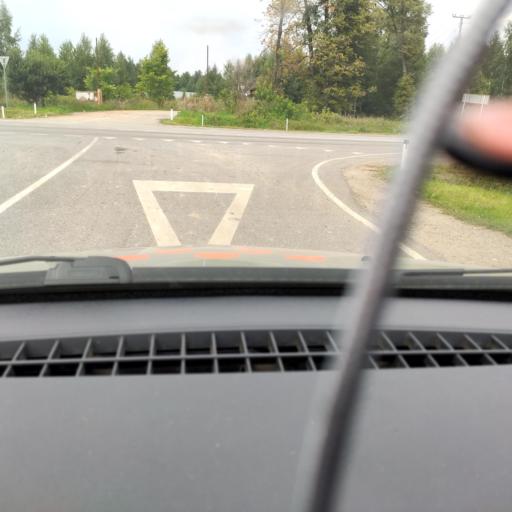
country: RU
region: Bashkortostan
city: Iglino
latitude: 54.7860
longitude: 56.5372
